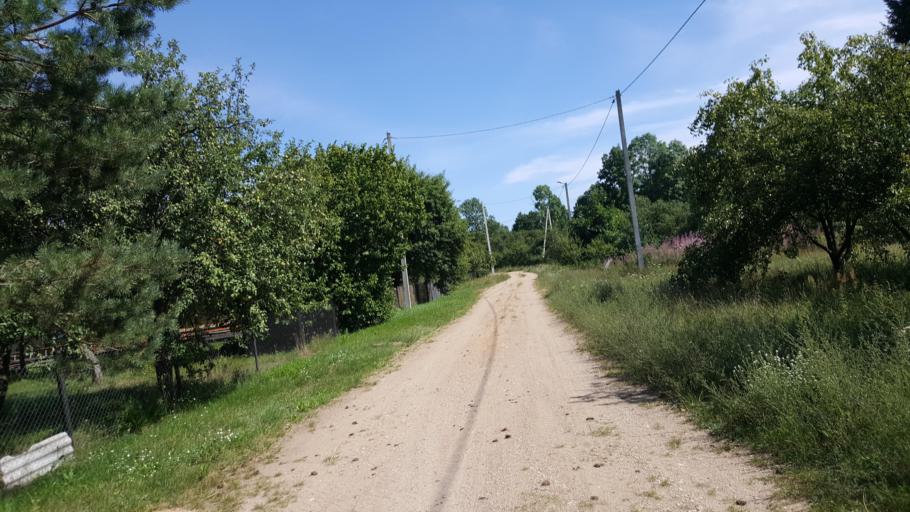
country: BY
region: Brest
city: Zhabinka
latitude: 52.4629
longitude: 24.1028
